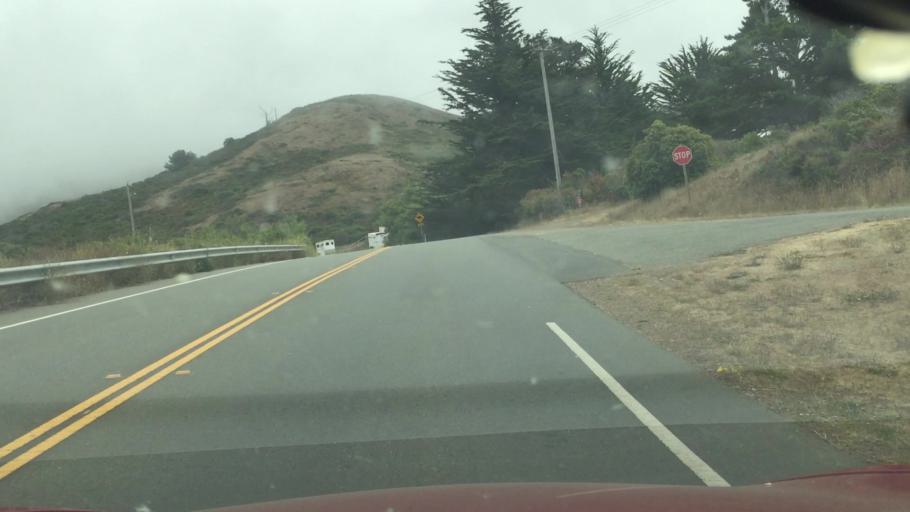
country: US
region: California
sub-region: Marin County
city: Marin City
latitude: 37.8324
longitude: -122.5171
